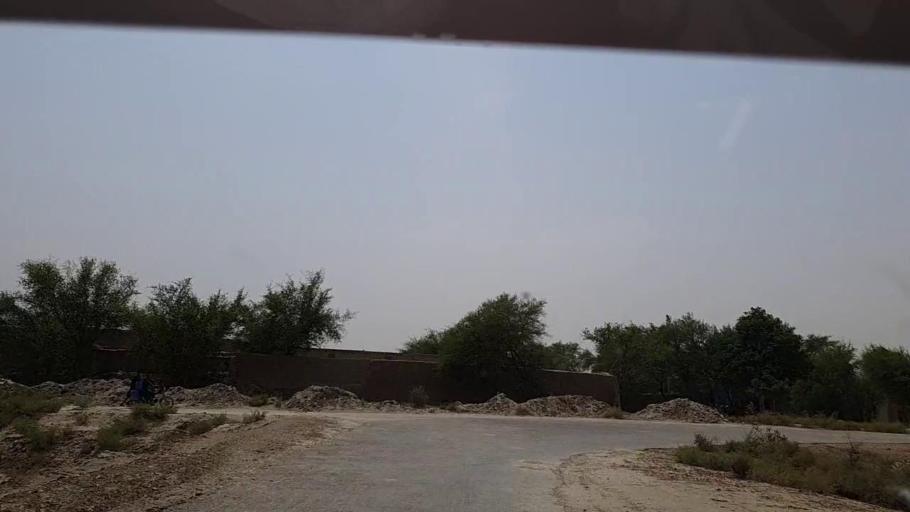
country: PK
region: Sindh
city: Phulji
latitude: 27.0175
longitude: 67.5847
